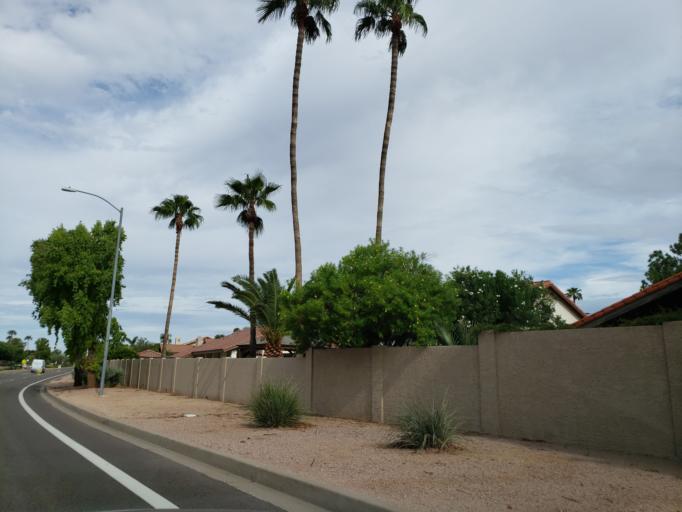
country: US
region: Arizona
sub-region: Maricopa County
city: Paradise Valley
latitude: 33.5728
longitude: -111.8977
